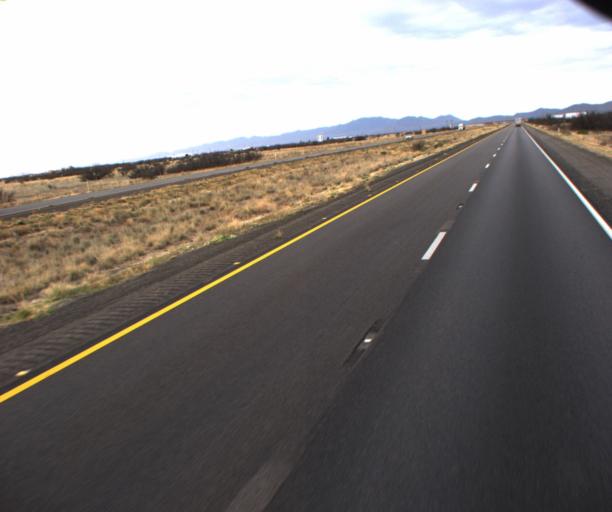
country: US
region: Arizona
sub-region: Cochise County
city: Willcox
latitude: 32.2343
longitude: -109.8691
